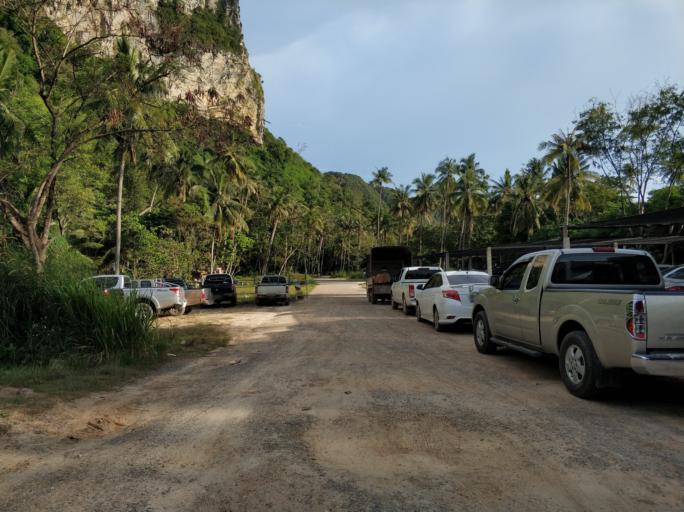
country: TH
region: Phangnga
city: Ban Ao Nang
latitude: 8.0291
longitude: 98.8258
